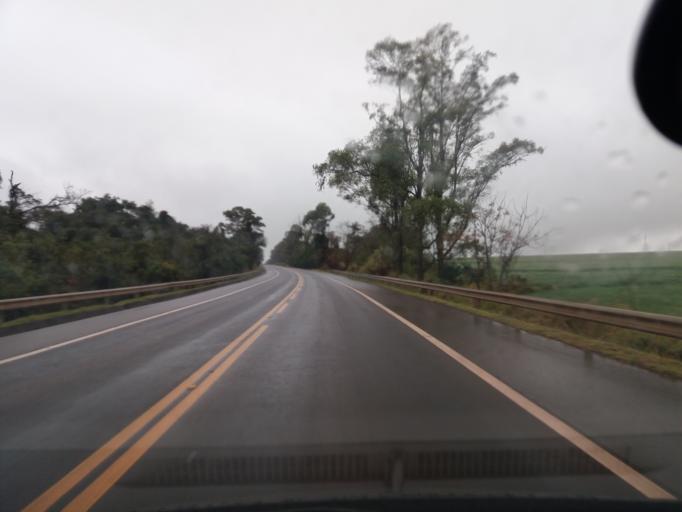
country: BR
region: Parana
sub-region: Campo Mourao
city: Campo Mourao
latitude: -24.3187
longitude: -52.6264
